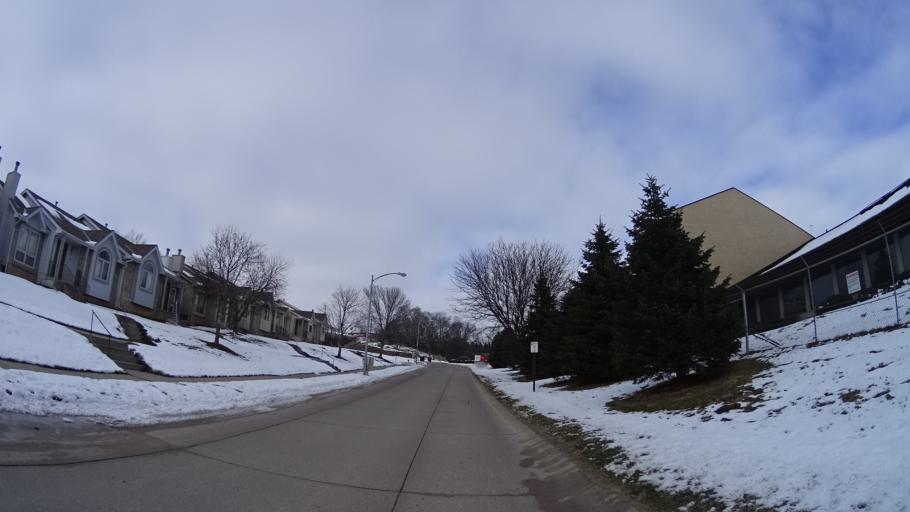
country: US
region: Nebraska
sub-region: Sarpy County
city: Offutt Air Force Base
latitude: 41.1175
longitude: -95.9515
